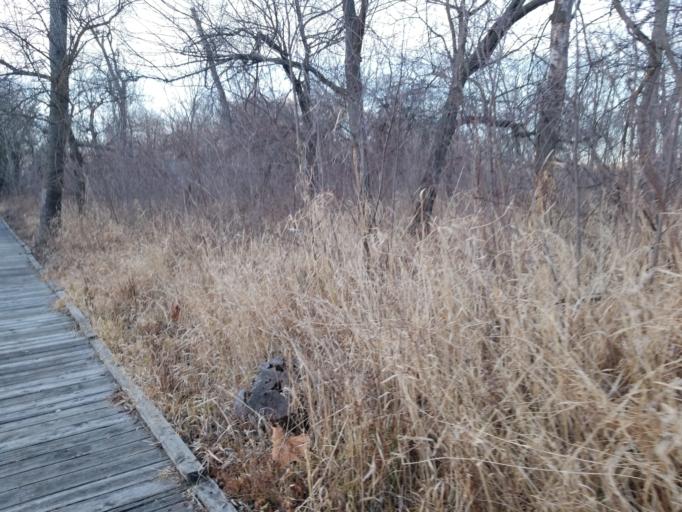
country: US
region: Nebraska
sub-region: Sarpy County
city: Bellevue
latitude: 41.1740
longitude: -95.8899
